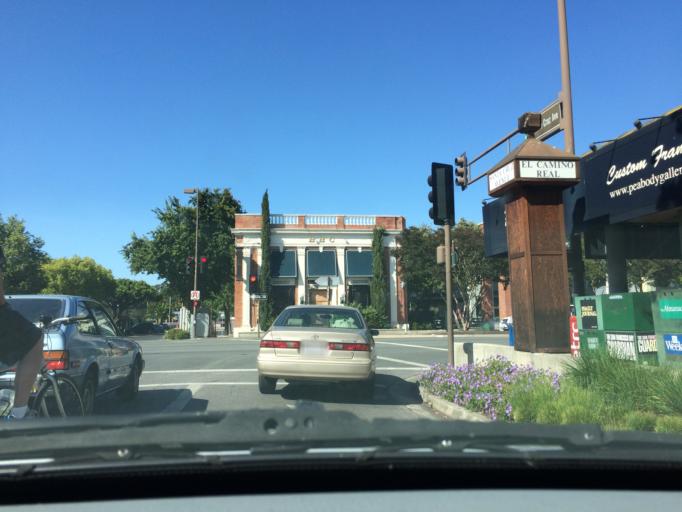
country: US
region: California
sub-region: San Mateo County
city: Menlo Park
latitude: 37.4533
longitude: -122.1831
